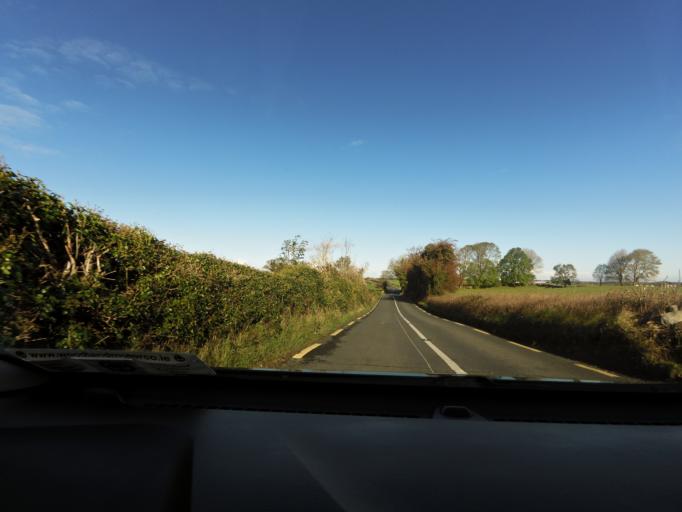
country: IE
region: Connaught
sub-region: Maigh Eo
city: Ballinrobe
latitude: 53.5115
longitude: -9.0816
